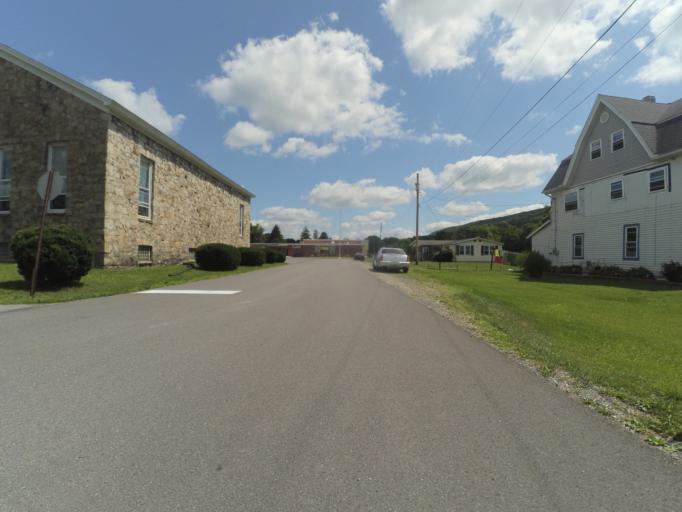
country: US
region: Pennsylvania
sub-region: Centre County
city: Stormstown
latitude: 40.7993
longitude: -78.0512
